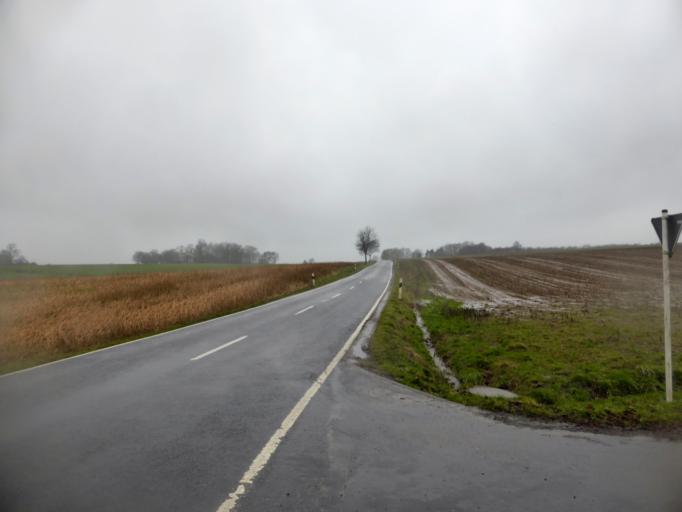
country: LU
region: Diekirch
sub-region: Canton de Redange
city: Ell
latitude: 49.7601
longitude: 5.8368
